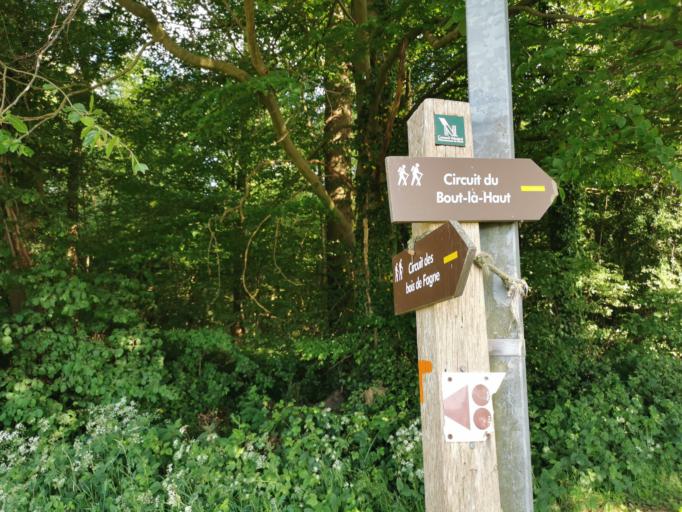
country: FR
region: Nord-Pas-de-Calais
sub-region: Departement du Nord
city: Marpent
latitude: 50.2251
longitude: 4.1024
